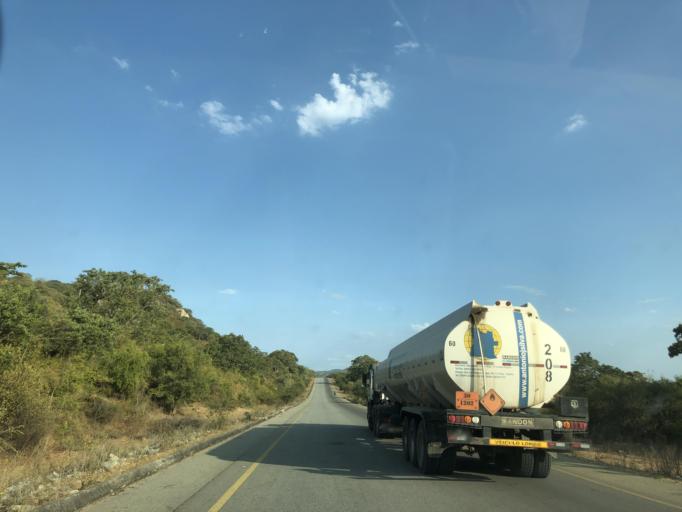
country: AO
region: Benguela
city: Benguela
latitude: -13.3571
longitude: 13.8497
